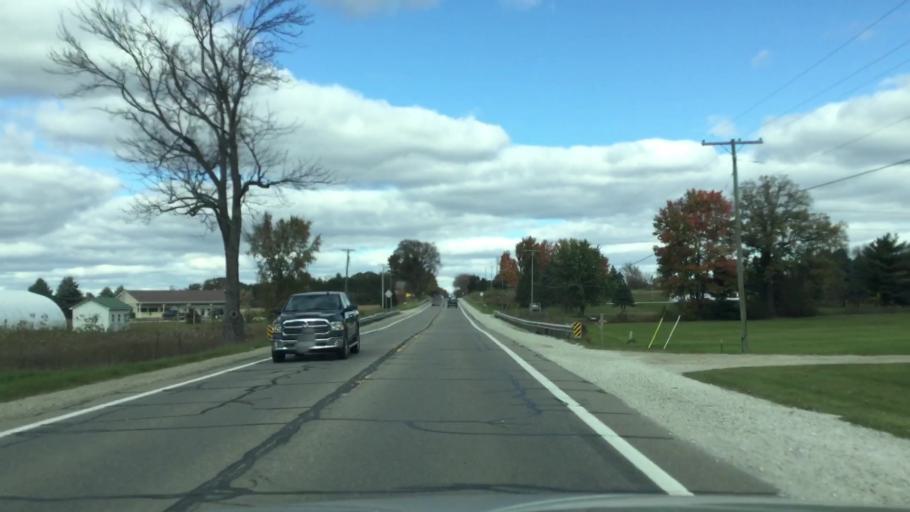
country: US
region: Michigan
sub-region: Lapeer County
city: Lapeer
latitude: 43.0954
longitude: -83.3079
